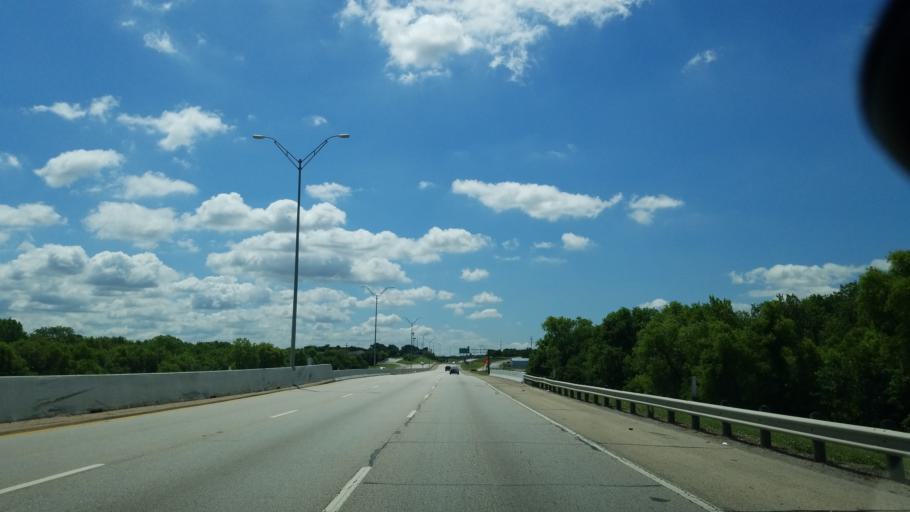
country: US
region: Texas
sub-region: Dallas County
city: Hutchins
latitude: 32.7385
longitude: -96.7182
